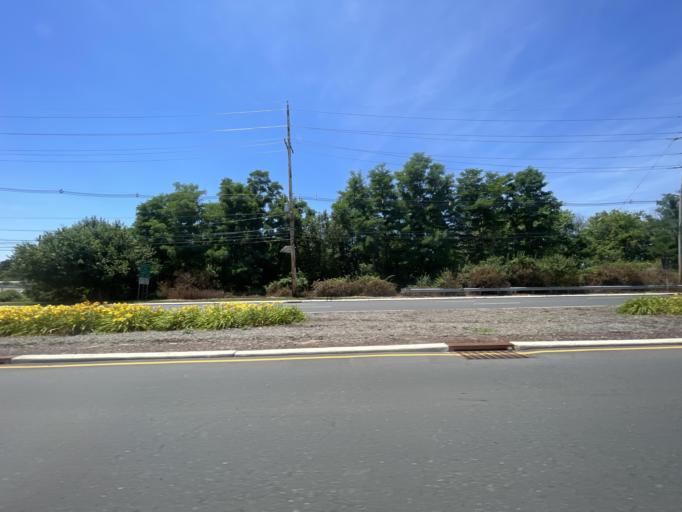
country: US
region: New Jersey
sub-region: Mercer County
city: Princeton Junction
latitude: 40.3258
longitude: -74.6419
